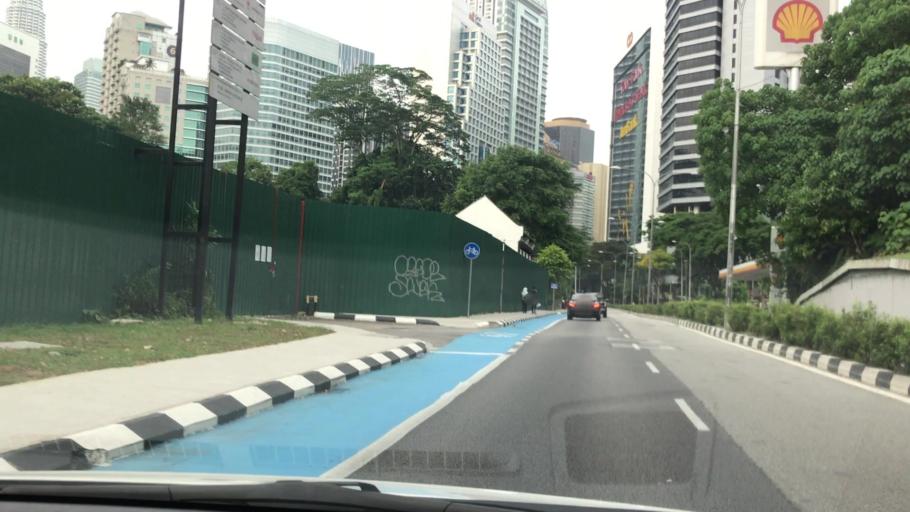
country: MY
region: Kuala Lumpur
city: Kuala Lumpur
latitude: 3.1501
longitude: 101.7033
